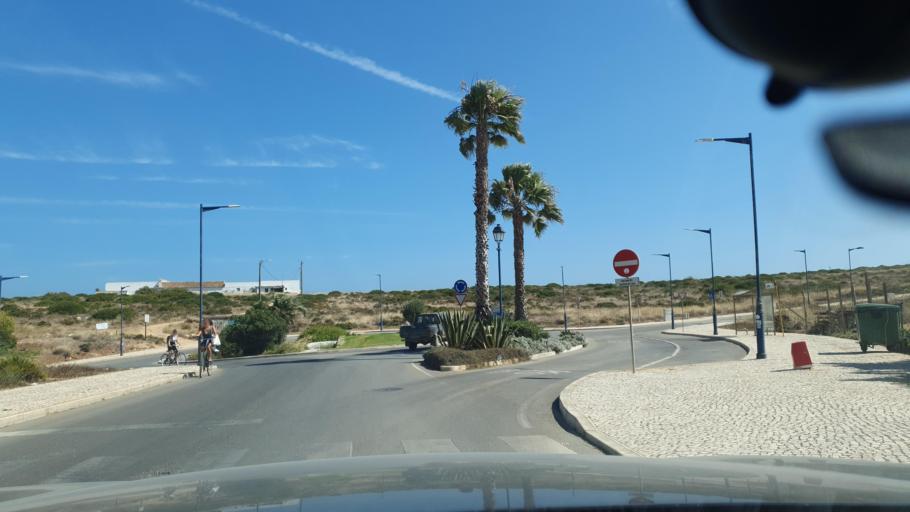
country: PT
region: Faro
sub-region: Vila do Bispo
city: Sagres
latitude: 37.0091
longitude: -8.9316
